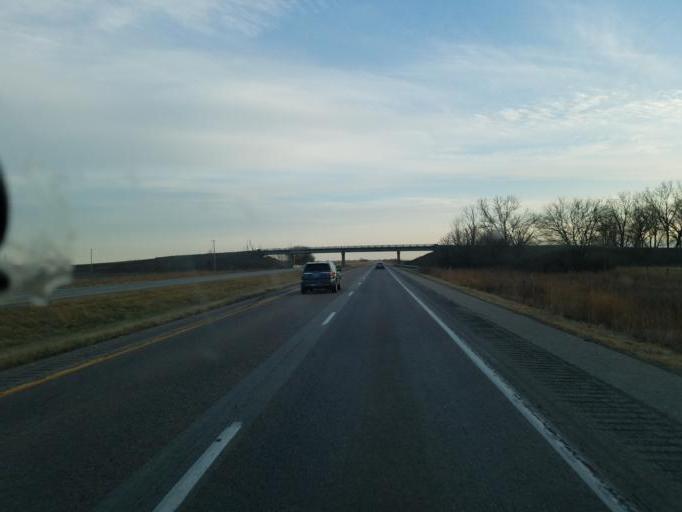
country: US
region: Nebraska
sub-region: Washington County
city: Blair
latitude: 41.6702
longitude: -96.0358
